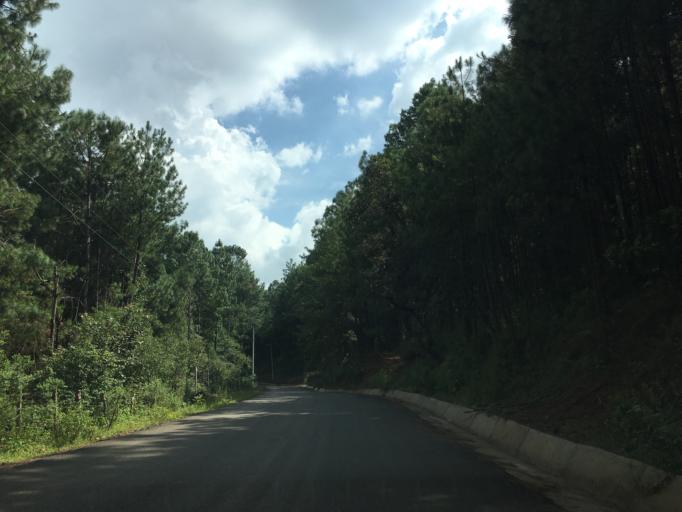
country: MX
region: Michoacan
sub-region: Morelia
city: Morelos
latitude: 19.5523
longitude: -101.1983
